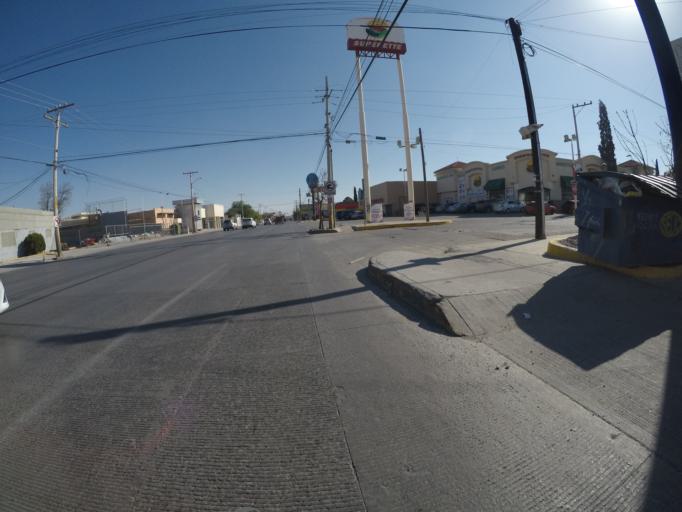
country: MX
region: Chihuahua
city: Ciudad Juarez
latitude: 31.7290
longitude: -106.4503
